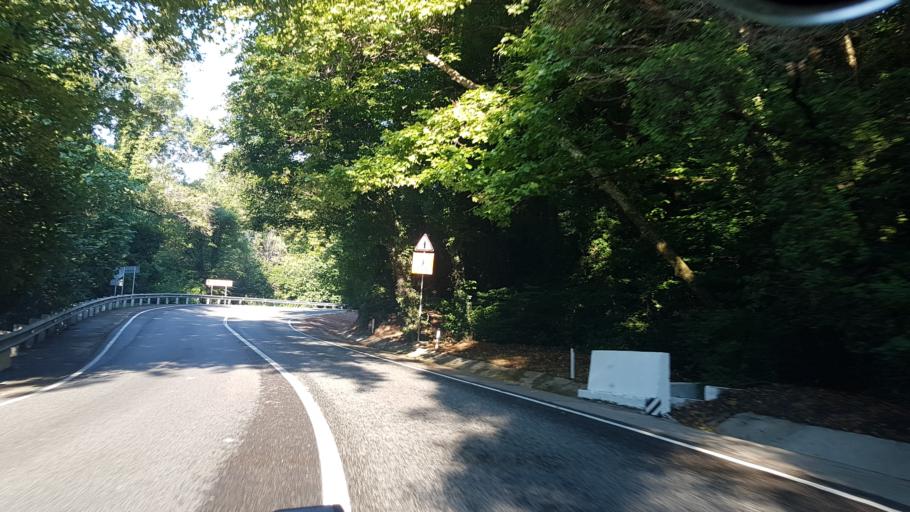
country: RU
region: Krasnodarskiy
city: Gornoye Loo
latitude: 43.6682
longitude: 39.6172
